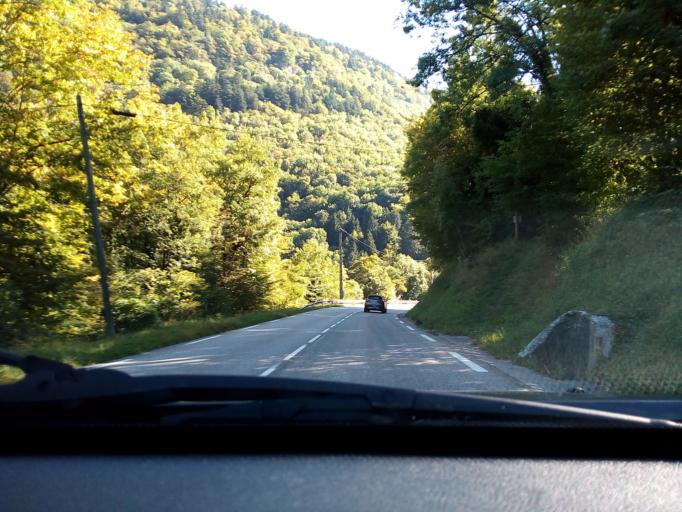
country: FR
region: Rhone-Alpes
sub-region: Departement de l'Isere
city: Sassenage
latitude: 45.2007
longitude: 5.6318
